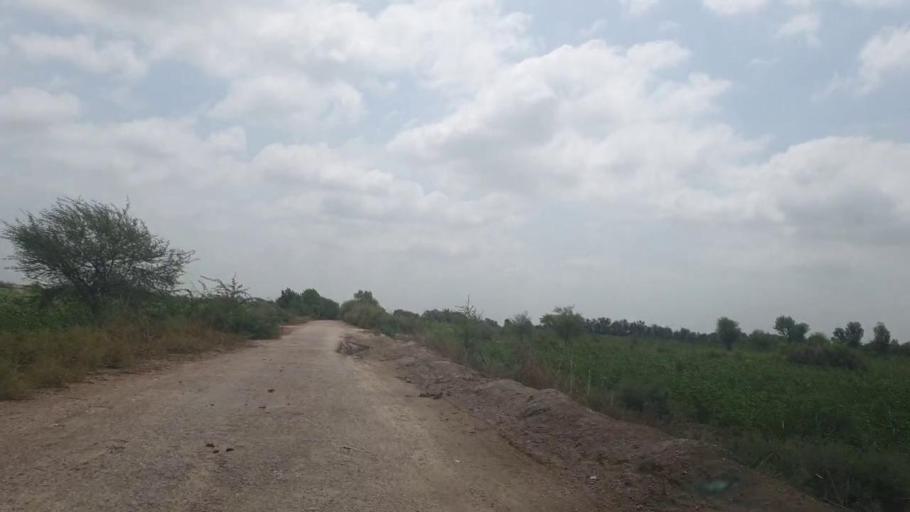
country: PK
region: Sindh
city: Tando Mittha Khan
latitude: 25.8870
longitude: 69.1405
